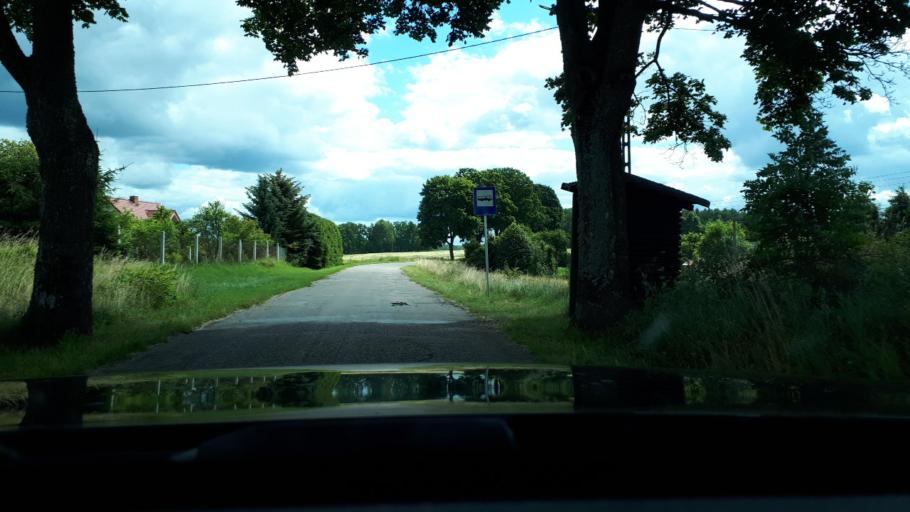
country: PL
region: Warmian-Masurian Voivodeship
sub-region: Powiat olsztynski
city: Olsztynek
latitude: 53.6344
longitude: 20.1909
